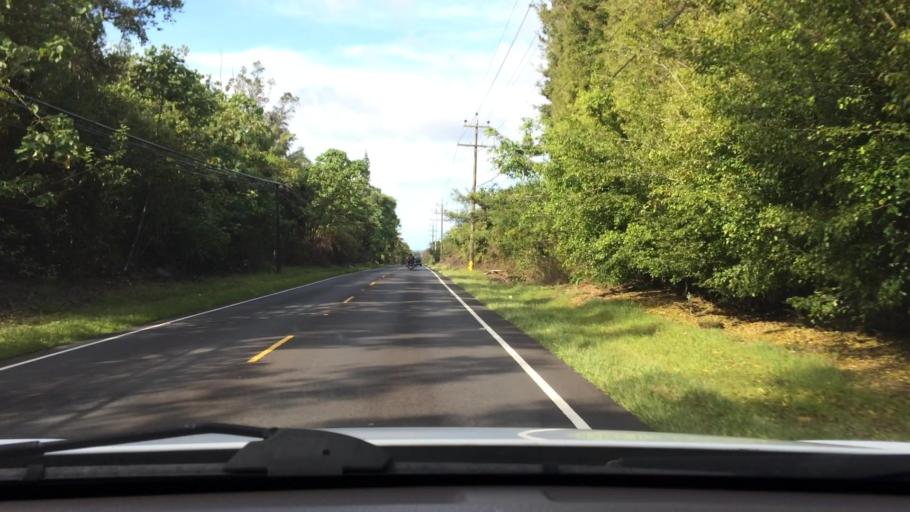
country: US
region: Hawaii
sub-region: Hawaii County
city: Hawaiian Paradise Park
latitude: 19.5099
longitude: -154.9455
